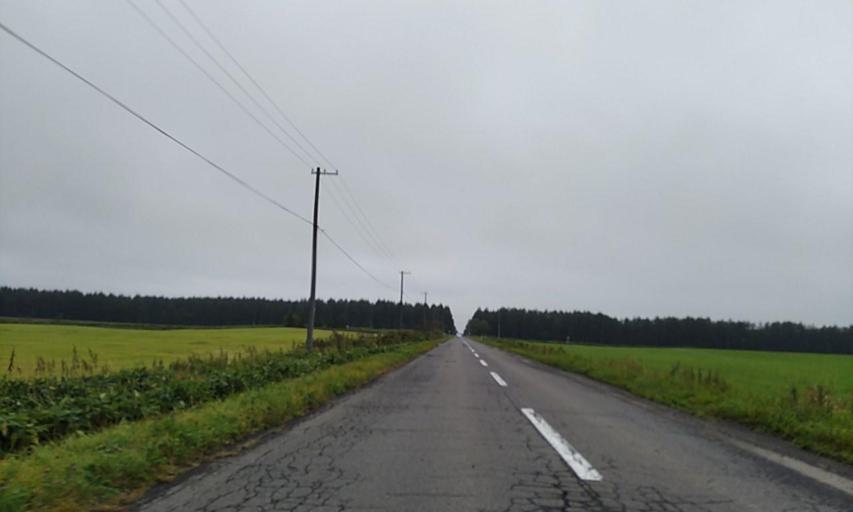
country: JP
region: Hokkaido
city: Shibetsu
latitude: 43.5460
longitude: 144.6979
